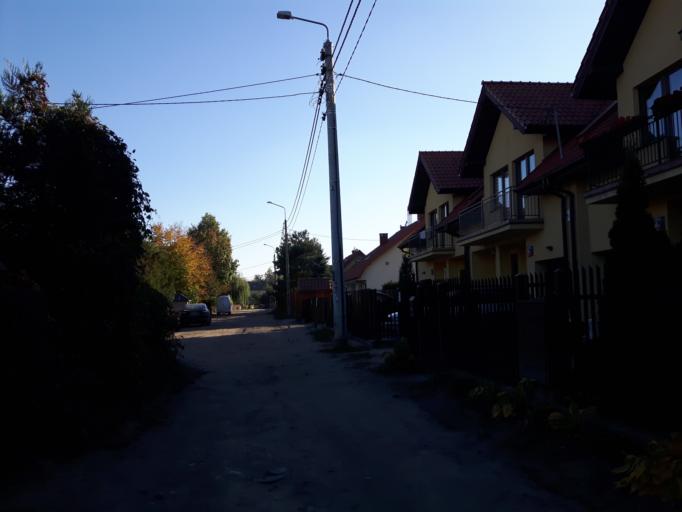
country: PL
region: Masovian Voivodeship
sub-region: Powiat wolominski
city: Zabki
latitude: 52.2836
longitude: 21.1321
